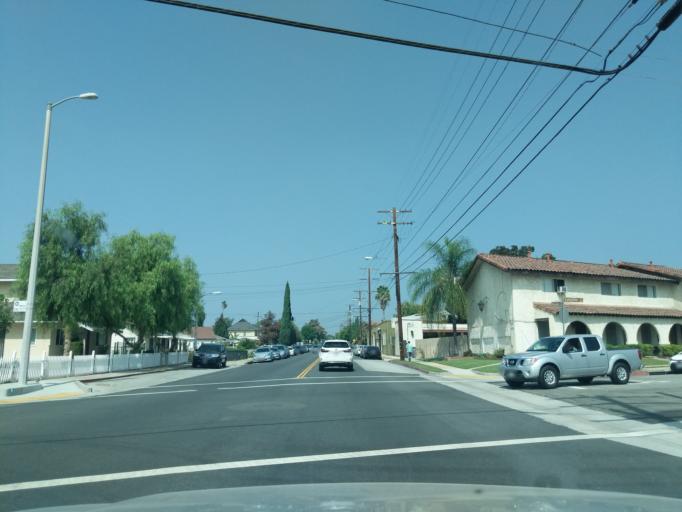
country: US
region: California
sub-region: Los Angeles County
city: East San Gabriel
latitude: 34.0925
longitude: -118.0950
